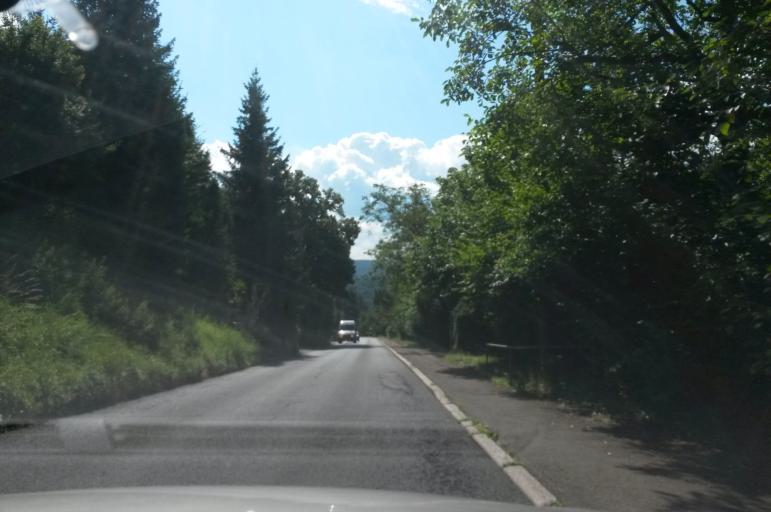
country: DE
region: Baden-Wuerttemberg
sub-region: Karlsruhe Region
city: Ispringen
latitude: 48.8944
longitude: 8.6630
